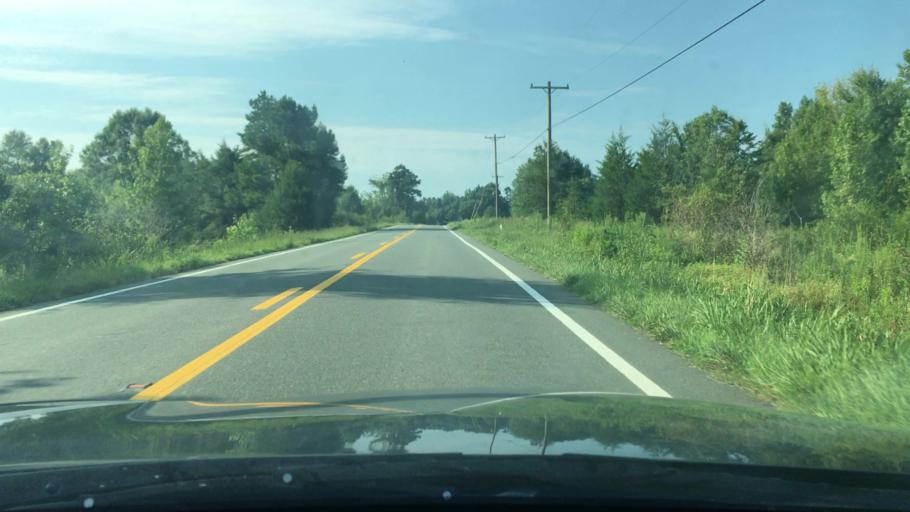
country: US
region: North Carolina
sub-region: Alamance County
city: Green Level
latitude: 36.2326
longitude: -79.3223
